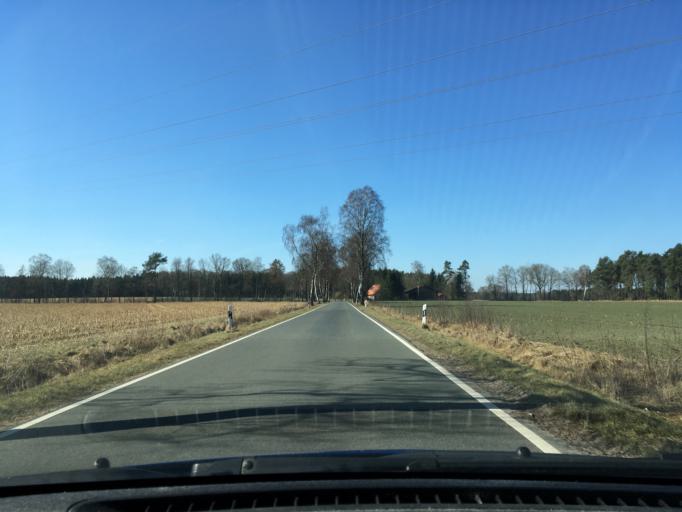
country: DE
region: Lower Saxony
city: Neuenkirchen
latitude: 53.0837
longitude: 9.7406
